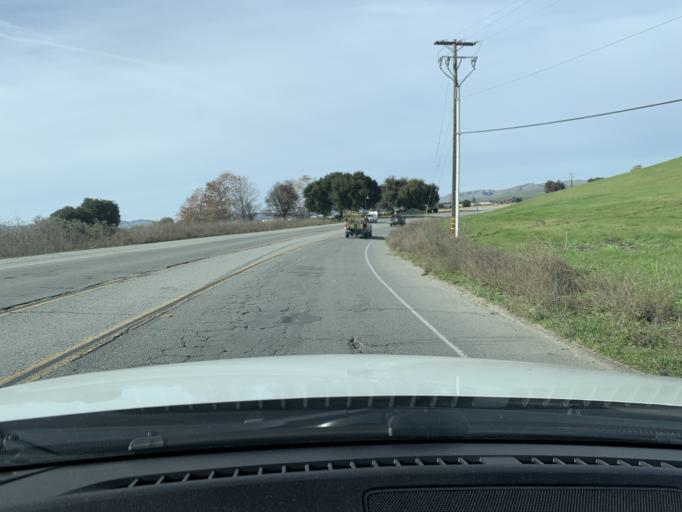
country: US
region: California
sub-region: San Benito County
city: Hollister
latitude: 36.8381
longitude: -121.4553
